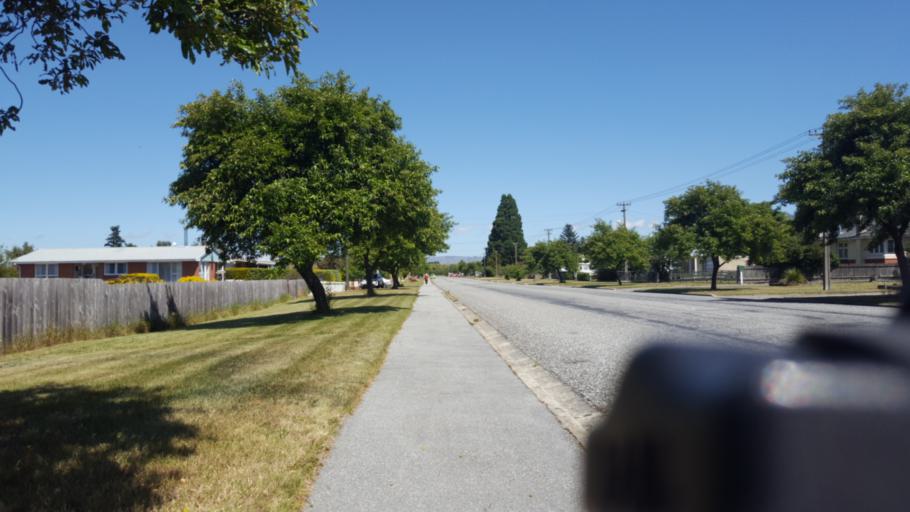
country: NZ
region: Otago
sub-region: Dunedin City
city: Dunedin
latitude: -45.1269
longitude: 170.1059
